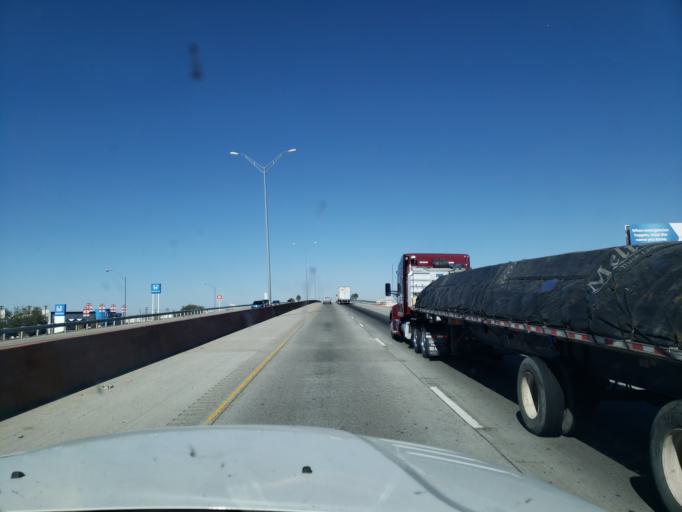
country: US
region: Texas
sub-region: El Paso County
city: Canutillo
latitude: 31.8597
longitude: -106.5762
